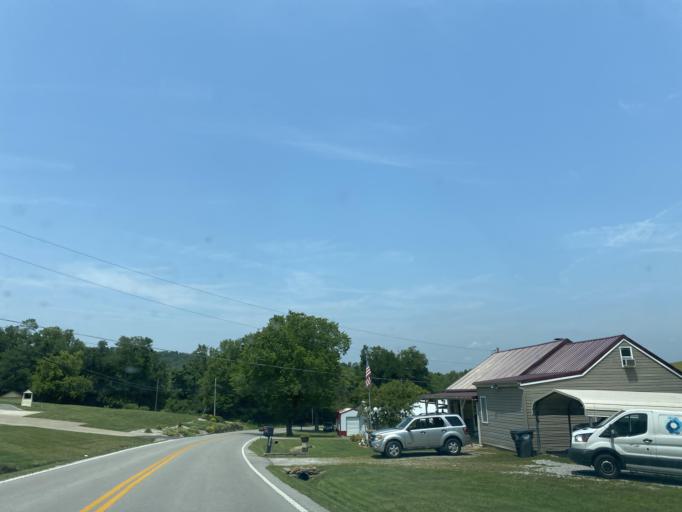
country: US
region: Kentucky
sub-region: Kenton County
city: Ryland Heights
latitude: 38.9072
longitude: -84.4486
